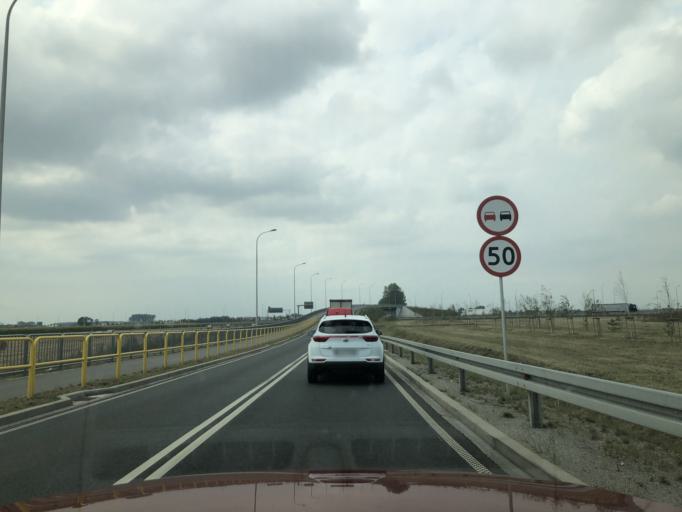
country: PL
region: Greater Poland Voivodeship
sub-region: Powiat leszczynski
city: Wilkowice
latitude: 51.8639
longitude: 16.5228
